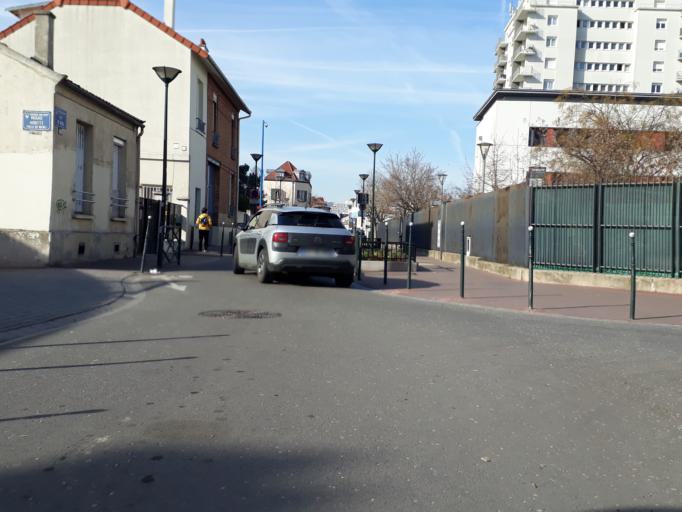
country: FR
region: Ile-de-France
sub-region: Departement des Hauts-de-Seine
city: Asnieres-sur-Seine
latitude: 48.9218
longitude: 2.2831
